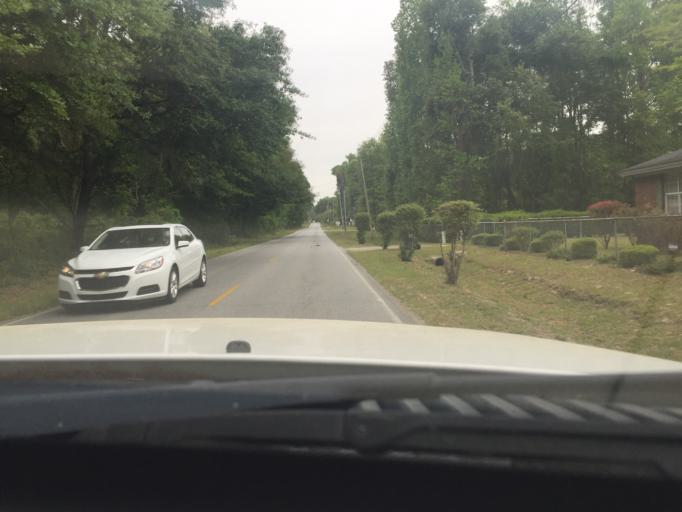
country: US
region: Georgia
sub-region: Chatham County
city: Georgetown
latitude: 31.9718
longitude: -81.2453
